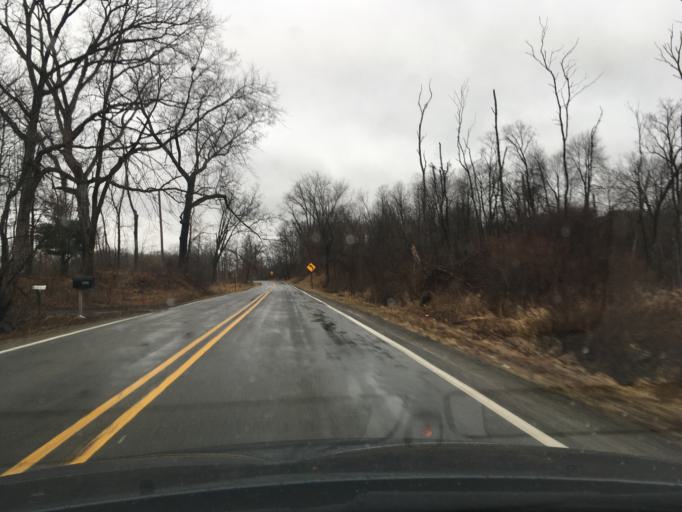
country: US
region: Michigan
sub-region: Washtenaw County
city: Chelsea
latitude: 42.3091
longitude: -84.0890
